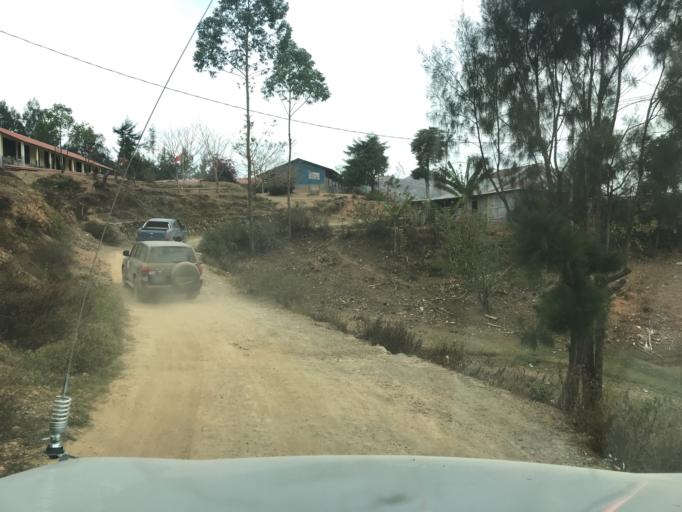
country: TL
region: Ermera
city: Gleno
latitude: -8.8286
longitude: 125.4537
